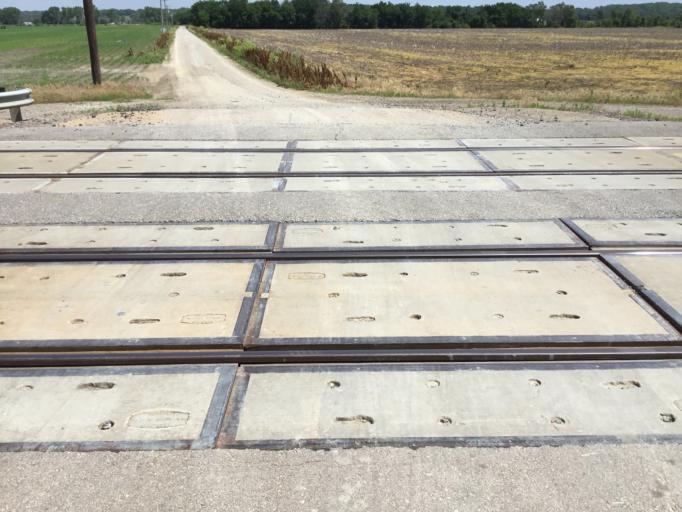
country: US
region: Kansas
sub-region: Shawnee County
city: Topeka
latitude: 39.0802
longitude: -95.5379
